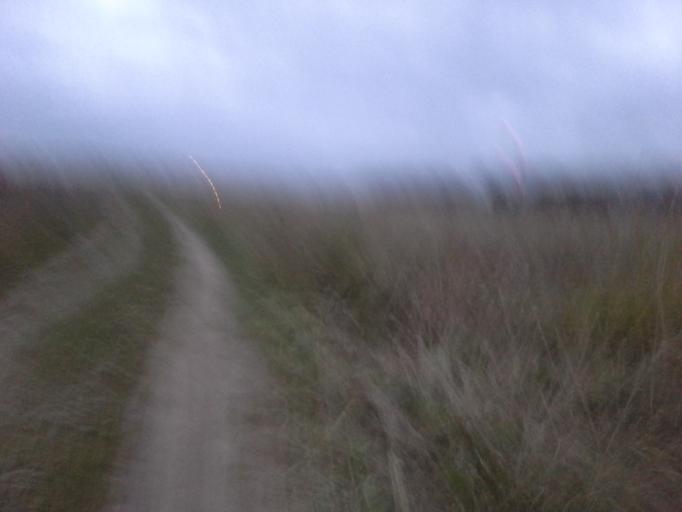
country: RU
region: Moskovskaya
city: Zhavoronki
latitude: 55.6455
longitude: 37.1315
